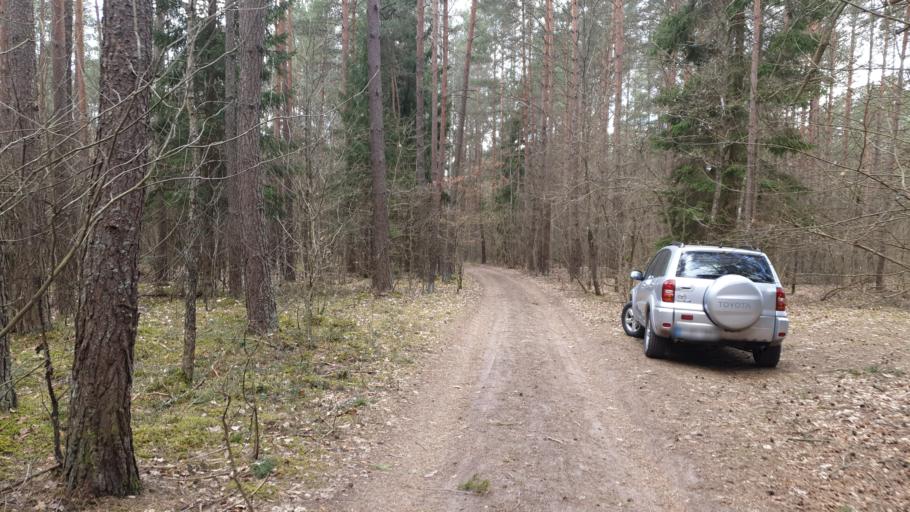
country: LT
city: Grigiskes
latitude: 54.7283
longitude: 25.0345
